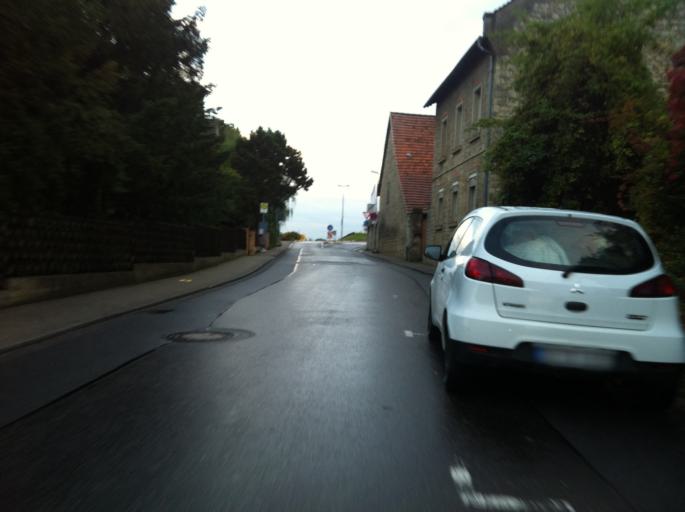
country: DE
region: Rheinland-Pfalz
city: Wackernheim
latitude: 49.9761
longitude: 8.1239
